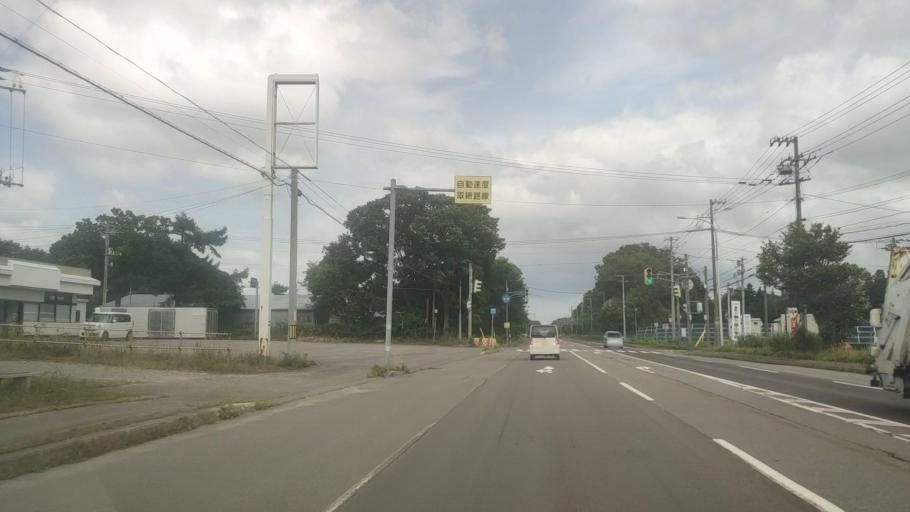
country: JP
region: Hokkaido
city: Nanae
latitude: 42.0362
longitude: 140.6072
